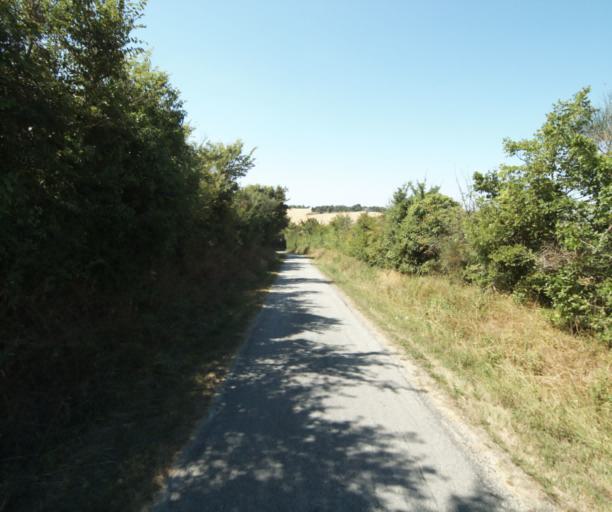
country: FR
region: Midi-Pyrenees
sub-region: Departement de la Haute-Garonne
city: Saint-Felix-Lauragais
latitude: 43.4911
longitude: 1.8942
